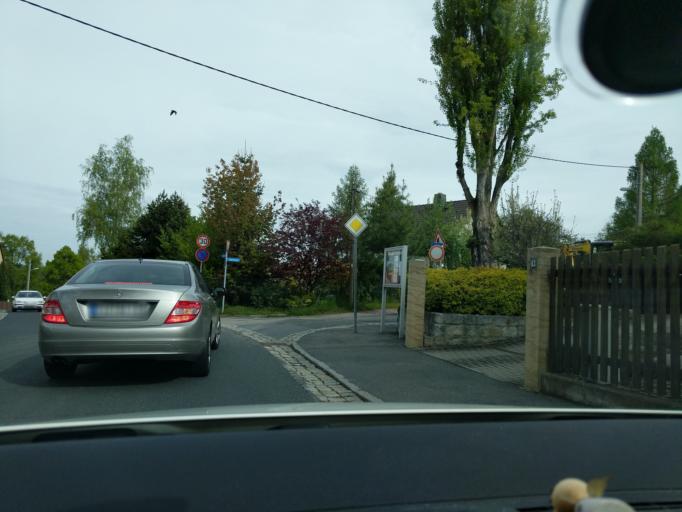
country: DE
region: Saxony
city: Bannewitz
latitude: 50.9921
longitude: 13.6954
